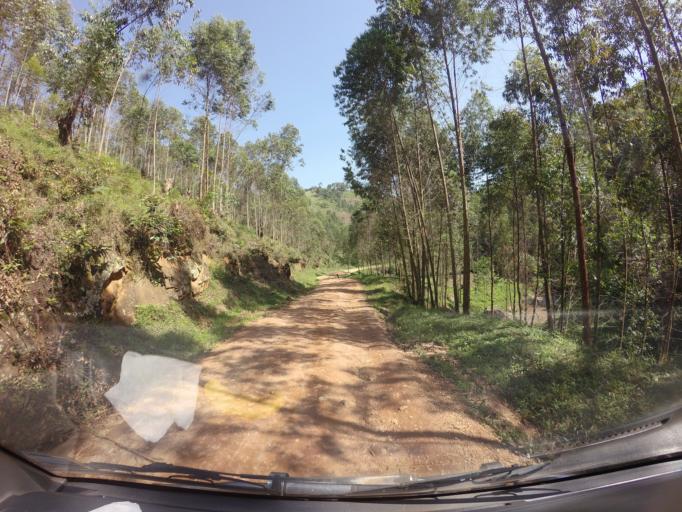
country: UG
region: Western Region
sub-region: Kanungu District
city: Kanungu
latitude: -0.8522
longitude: 29.7745
